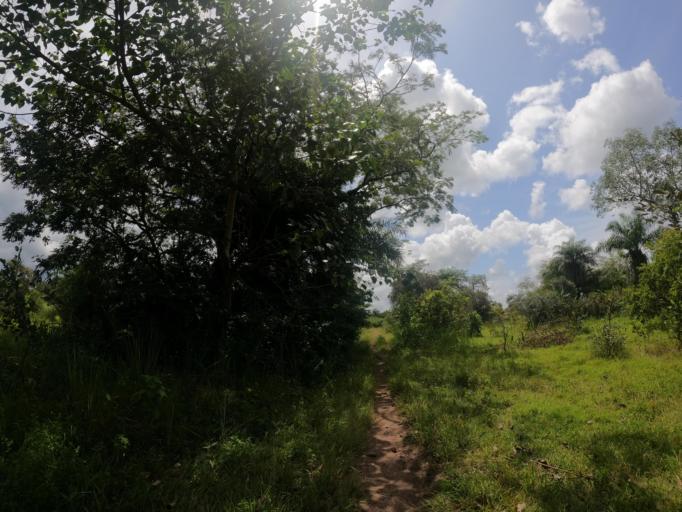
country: SL
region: Northern Province
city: Makeni
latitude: 9.1319
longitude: -12.2751
